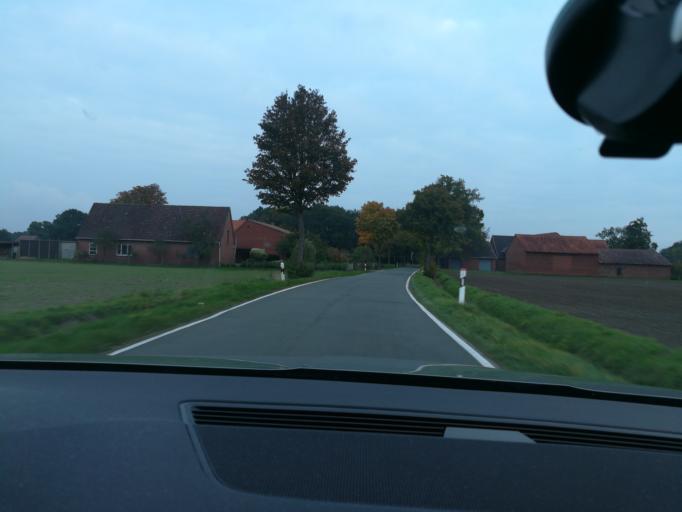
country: DE
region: Lower Saxony
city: Warmsen
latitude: 52.3738
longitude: 8.8606
